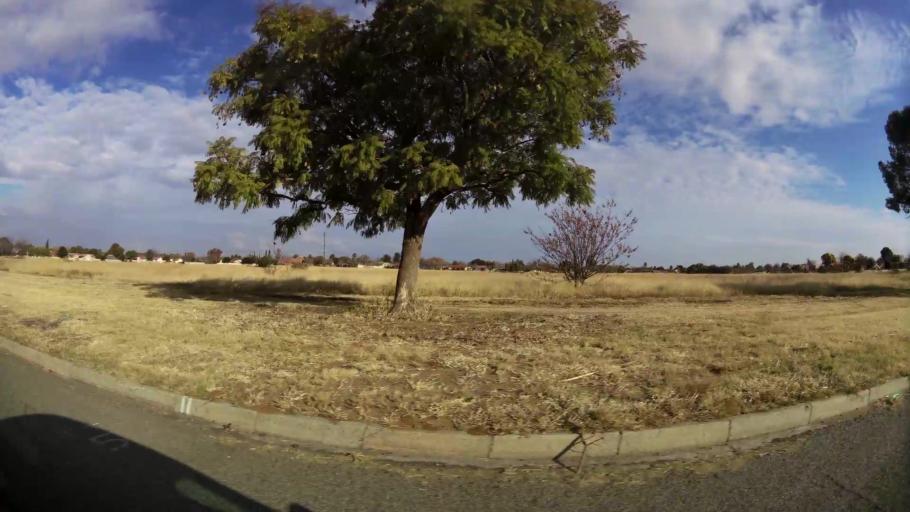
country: ZA
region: Orange Free State
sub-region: Lejweleputswa District Municipality
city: Welkom
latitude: -27.9748
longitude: 26.7026
